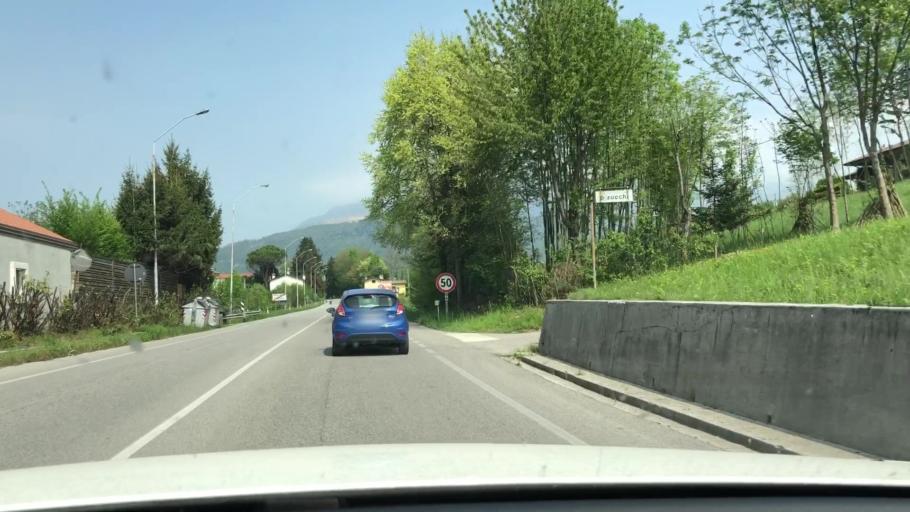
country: IT
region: Friuli Venezia Giulia
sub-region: Provincia di Udine
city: Cassacco
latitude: 46.1967
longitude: 13.1930
